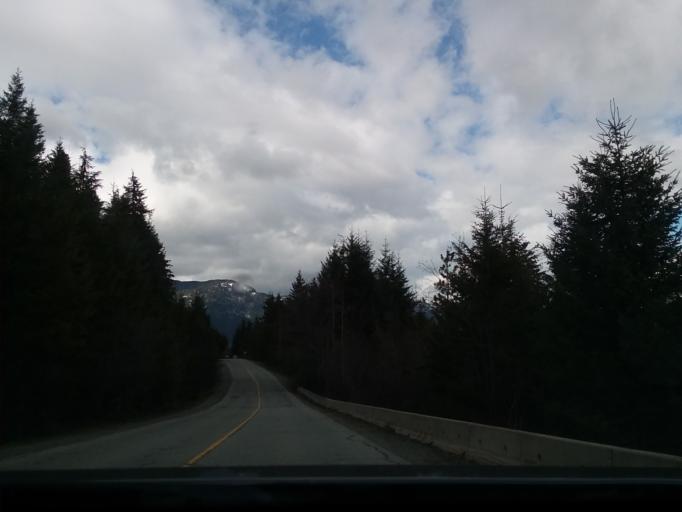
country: CA
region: British Columbia
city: Whistler
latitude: 50.1145
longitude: -122.9694
